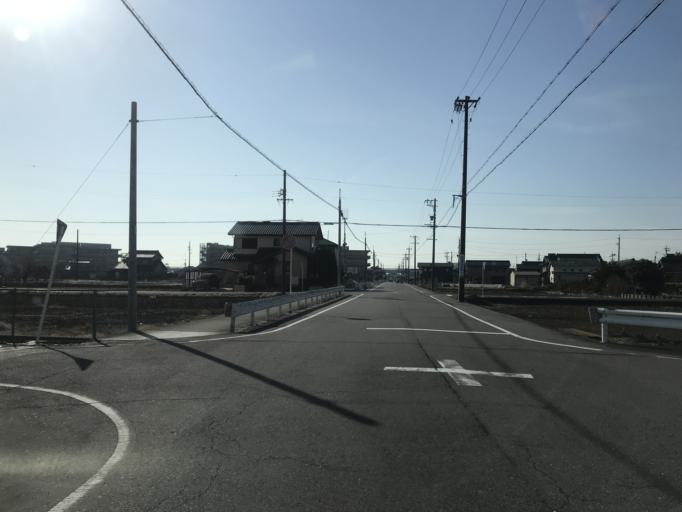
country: JP
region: Aichi
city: Iwakura
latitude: 35.2294
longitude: 136.8499
